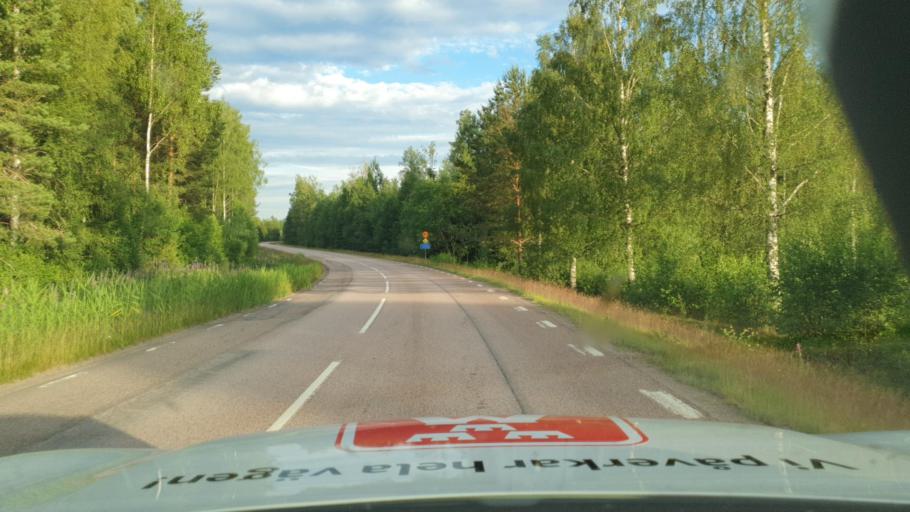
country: SE
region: Vaermland
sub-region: Karlstads Kommun
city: Molkom
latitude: 59.4978
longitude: 13.7983
